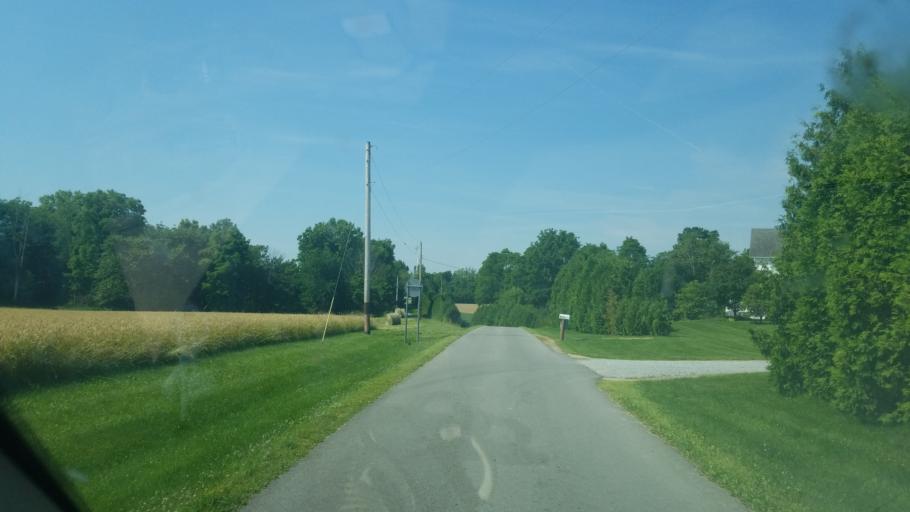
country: US
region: Ohio
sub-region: Wyandot County
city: Carey
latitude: 40.9587
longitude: -83.2822
